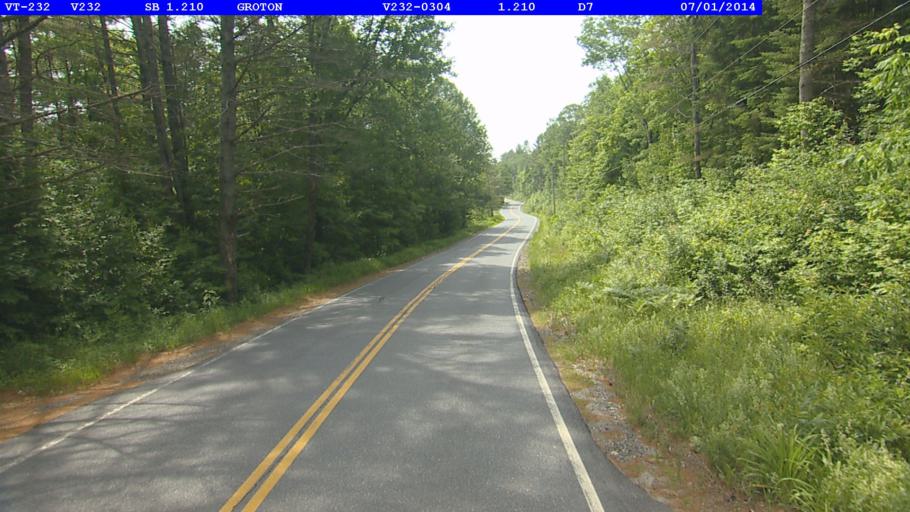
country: US
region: New Hampshire
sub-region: Grafton County
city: Woodsville
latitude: 44.2355
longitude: -72.2342
